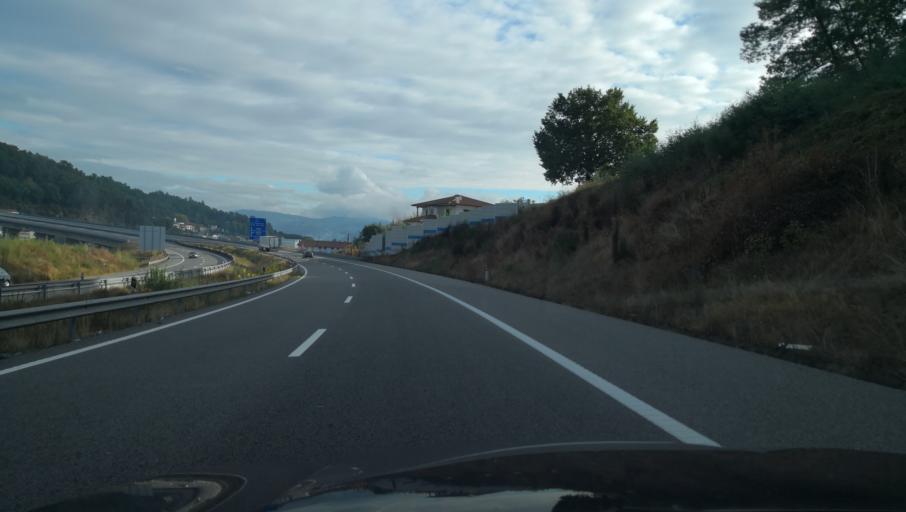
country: PT
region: Braga
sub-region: Guimaraes
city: Candoso
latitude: 41.4131
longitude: -8.3247
